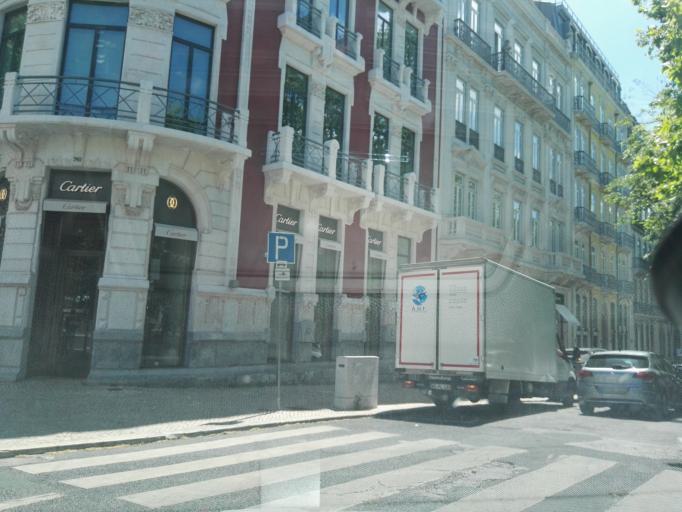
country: PT
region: Lisbon
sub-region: Lisbon
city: Lisbon
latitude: 38.7234
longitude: -9.1479
